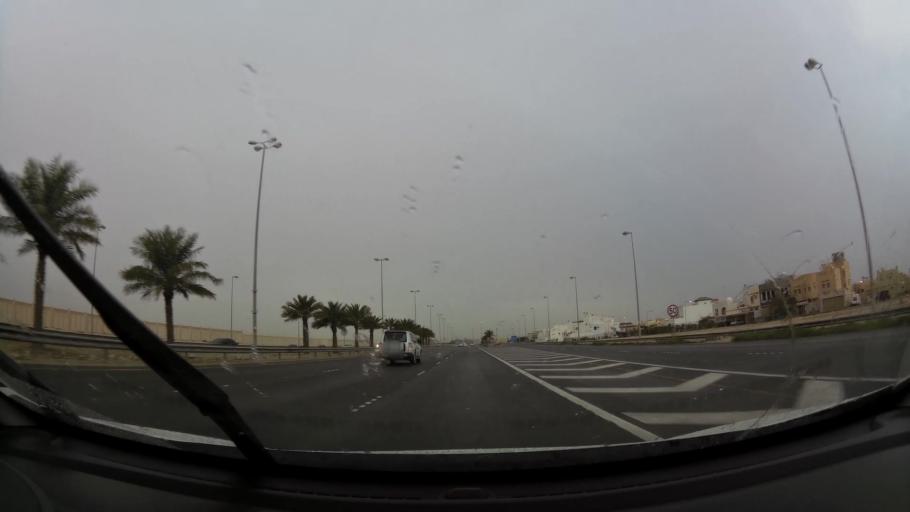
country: BH
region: Central Governorate
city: Madinat Hamad
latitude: 26.1042
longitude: 50.5110
